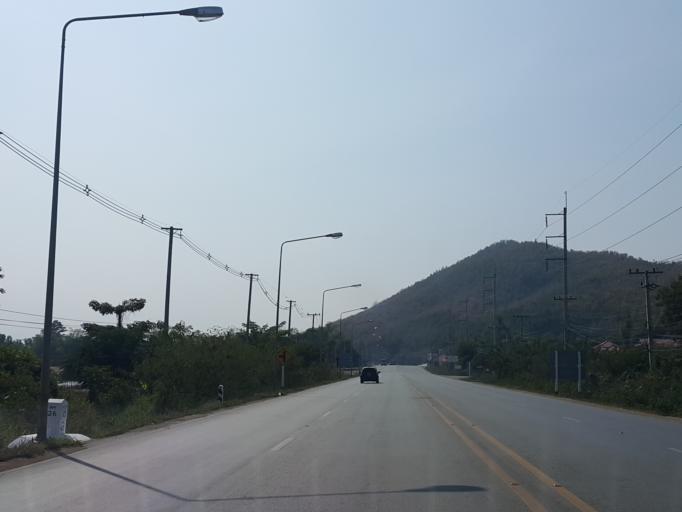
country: TH
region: Chiang Mai
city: Chom Thong
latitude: 18.3914
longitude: 98.6788
